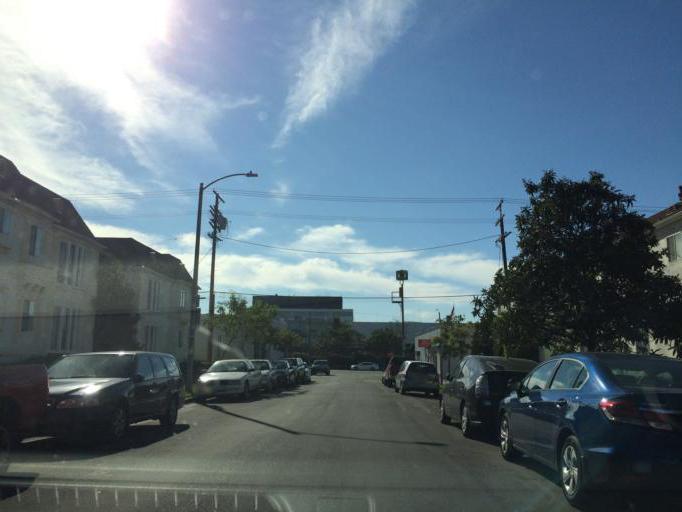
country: US
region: California
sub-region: Los Angeles County
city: West Hollywood
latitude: 34.0771
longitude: -118.3594
